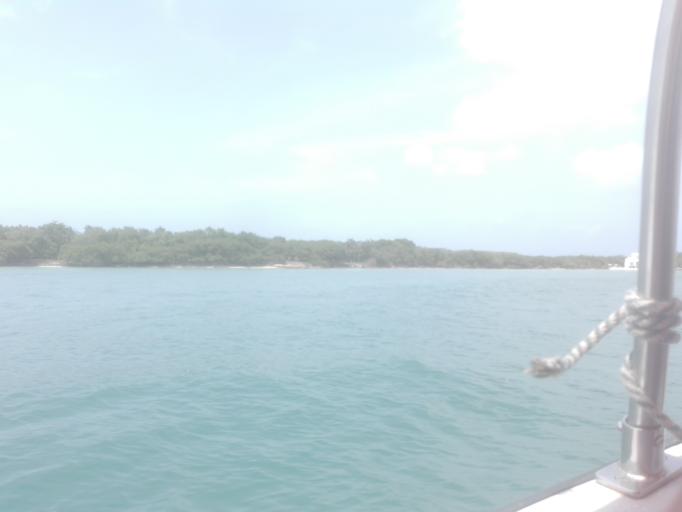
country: CO
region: Bolivar
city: Turbana
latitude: 10.1710
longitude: -75.6650
